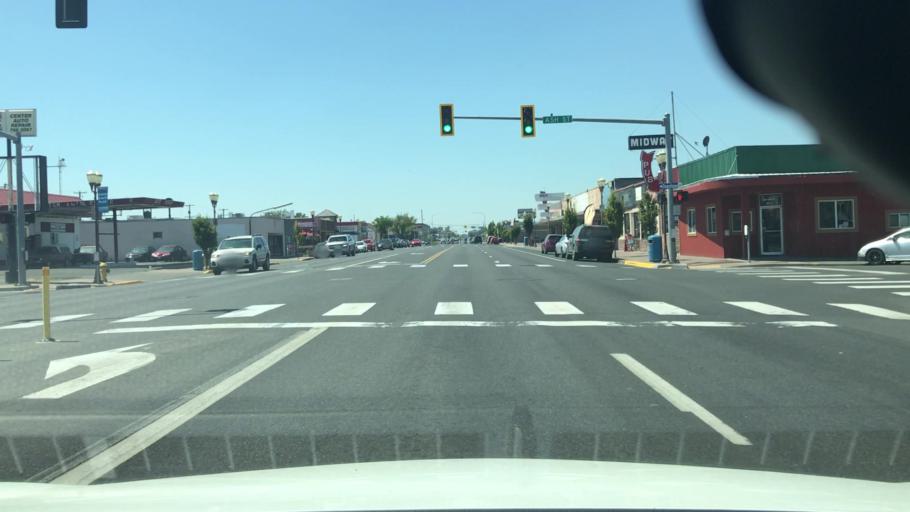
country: US
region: Washington
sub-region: Grant County
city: Moses Lake
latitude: 47.1305
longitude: -119.2801
